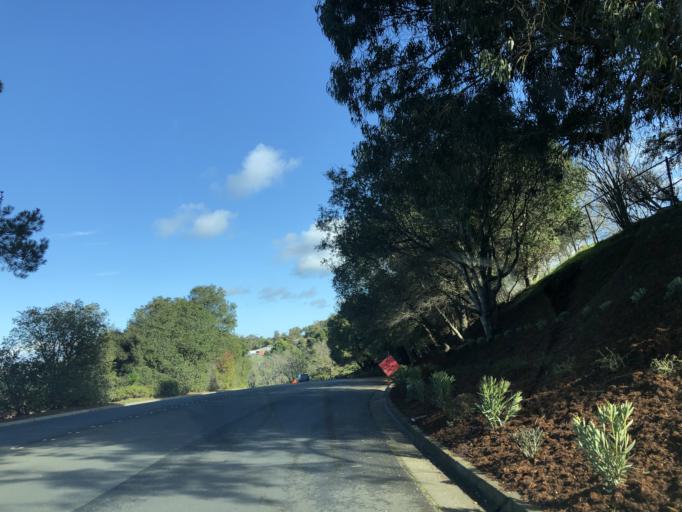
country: US
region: California
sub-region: Contra Costa County
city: Tara Hills
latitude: 37.9777
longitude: -122.3125
